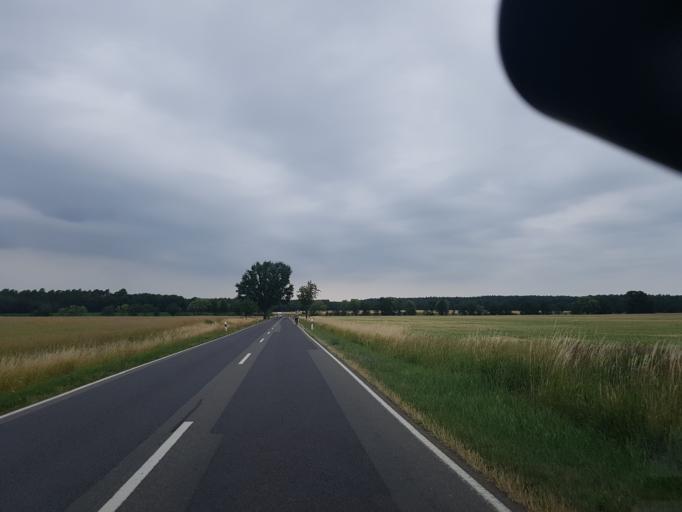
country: DE
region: Brandenburg
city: Lebusa
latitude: 51.8021
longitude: 13.4207
